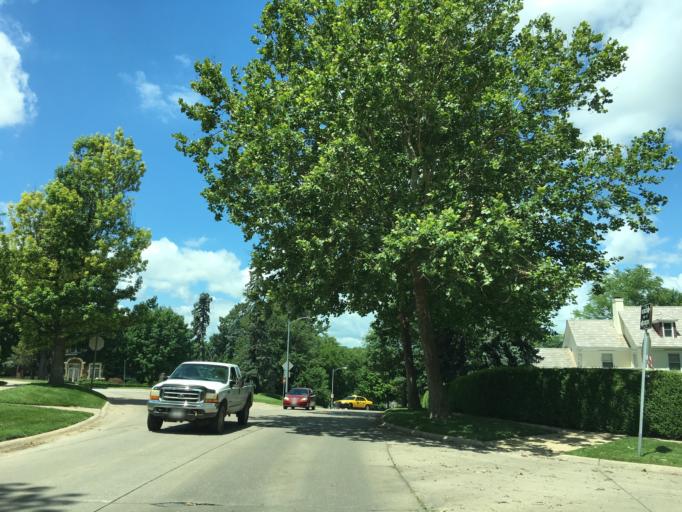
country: US
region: Nebraska
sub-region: Douglas County
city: Omaha
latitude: 41.2579
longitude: -95.9986
